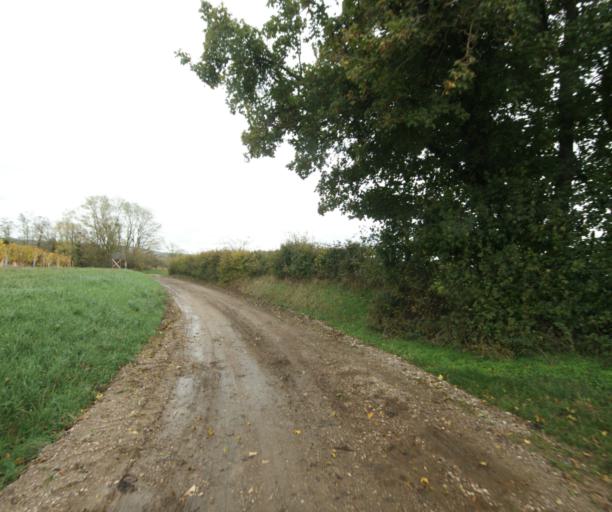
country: FR
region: Bourgogne
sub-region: Departement de Saone-et-Loire
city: Saint-Martin-Belle-Roche
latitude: 46.4719
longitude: 4.8530
